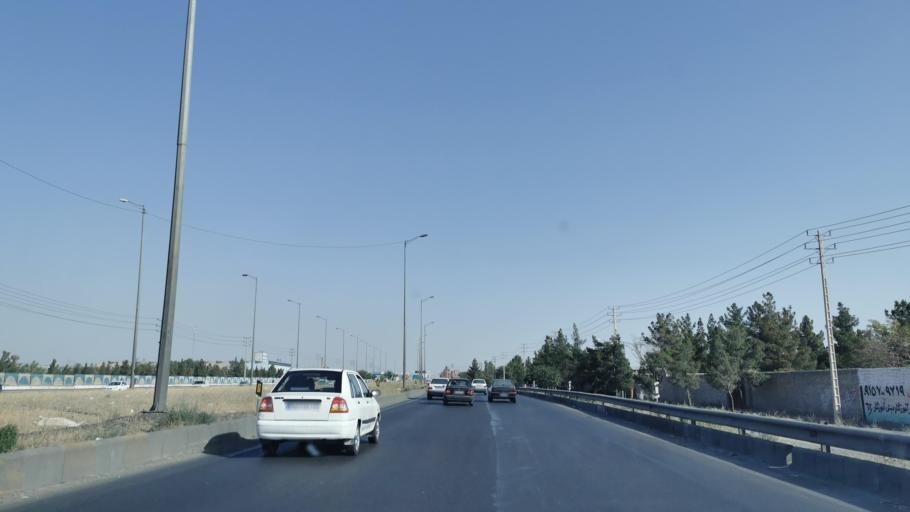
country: IR
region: Razavi Khorasan
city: Torqabeh
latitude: 36.4328
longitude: 59.4498
